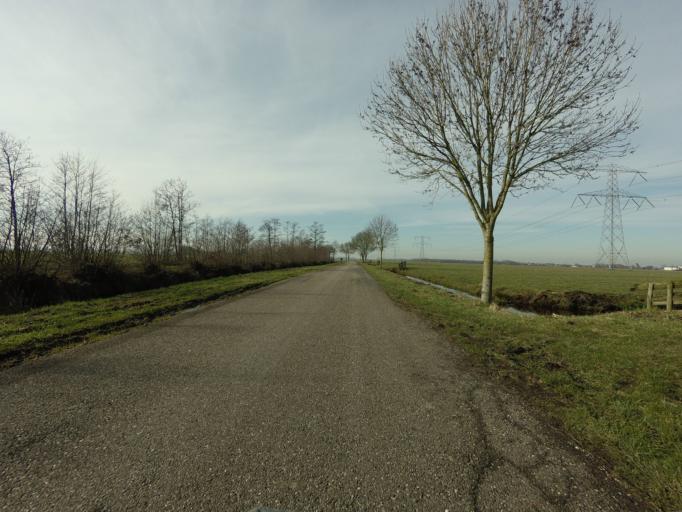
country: NL
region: South Holland
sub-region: Gemeente Sliedrecht
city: Sliedrecht
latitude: 51.8587
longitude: 4.7842
